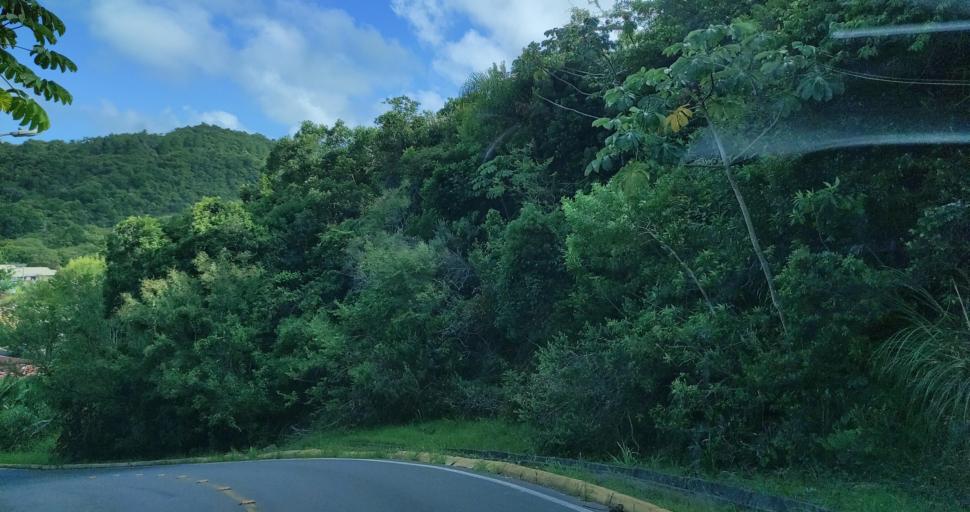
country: BR
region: Santa Catarina
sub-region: Porto Belo
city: Porto Belo
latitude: -27.1547
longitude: -48.4922
